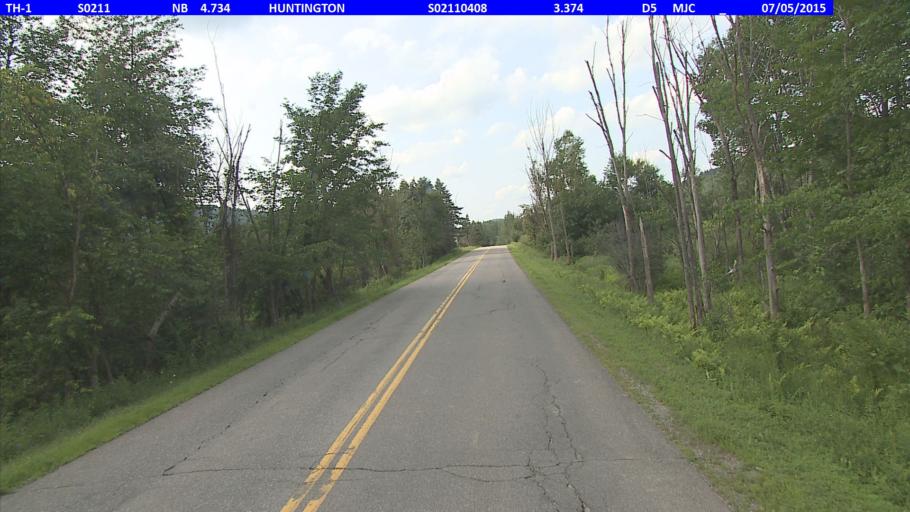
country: US
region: Vermont
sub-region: Chittenden County
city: Hinesburg
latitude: 44.2764
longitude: -72.9636
